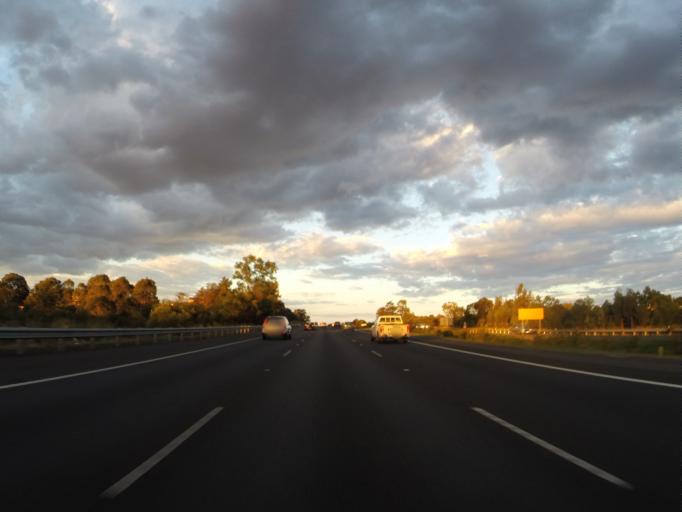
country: AU
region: New South Wales
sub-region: Campbelltown Municipality
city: Campbelltown
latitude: -34.0544
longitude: 150.8046
